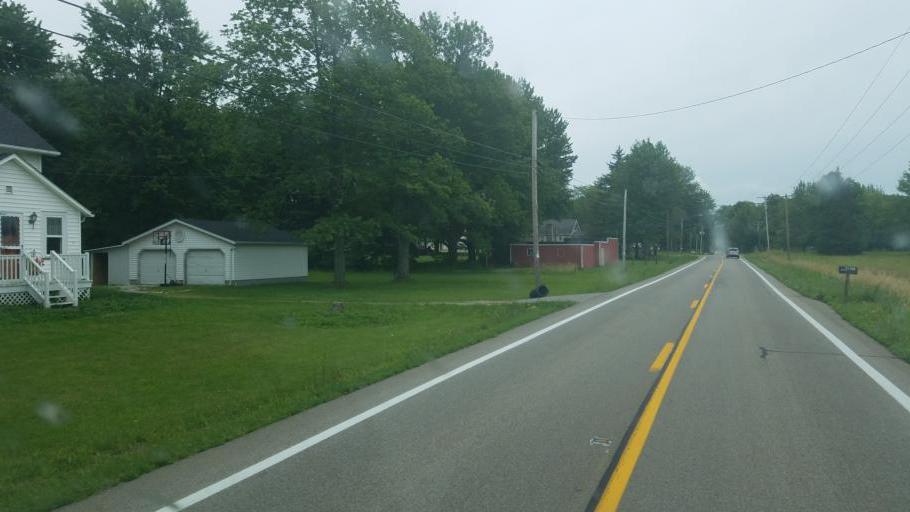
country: US
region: Ohio
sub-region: Ashtabula County
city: Orwell
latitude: 41.4616
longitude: -80.7933
